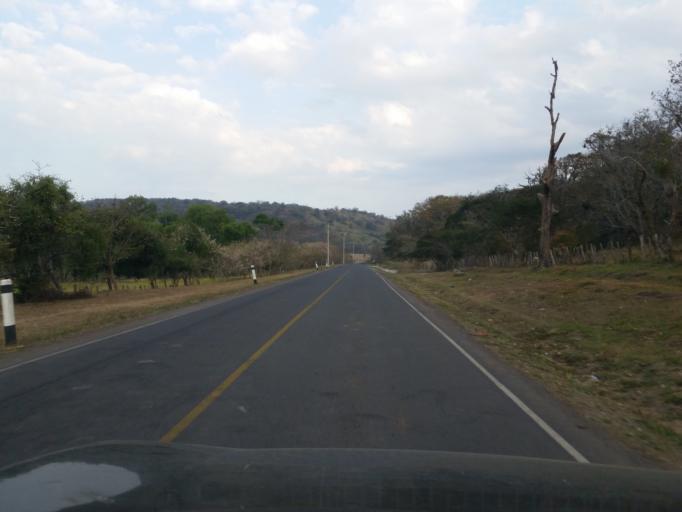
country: NI
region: Jinotega
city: San Rafael del Norte
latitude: 13.1733
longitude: -86.0721
